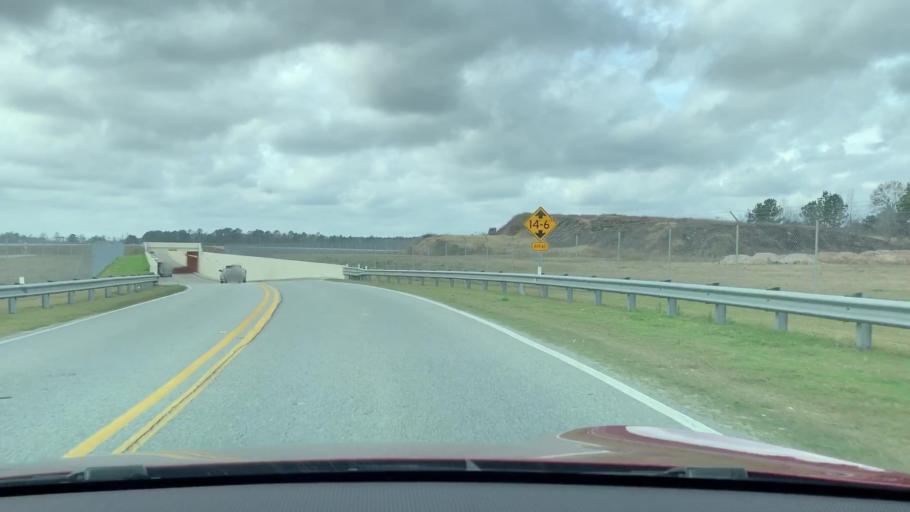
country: US
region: Georgia
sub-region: Chatham County
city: Port Wentworth
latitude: 32.1421
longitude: -81.2011
